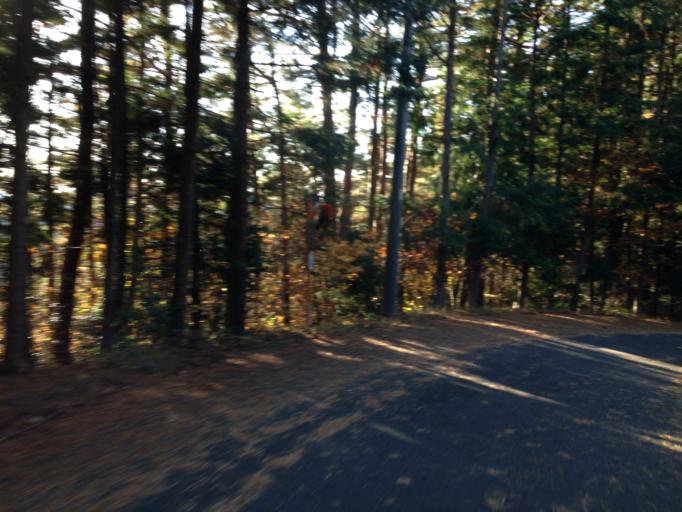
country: JP
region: Gifu
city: Mitake
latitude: 35.6130
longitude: 137.2155
